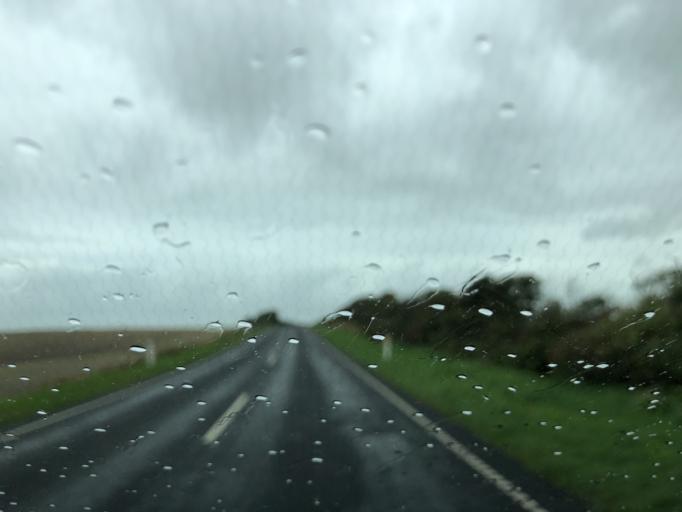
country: DK
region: North Denmark
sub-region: Thisted Kommune
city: Hurup
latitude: 56.7354
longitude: 8.3363
